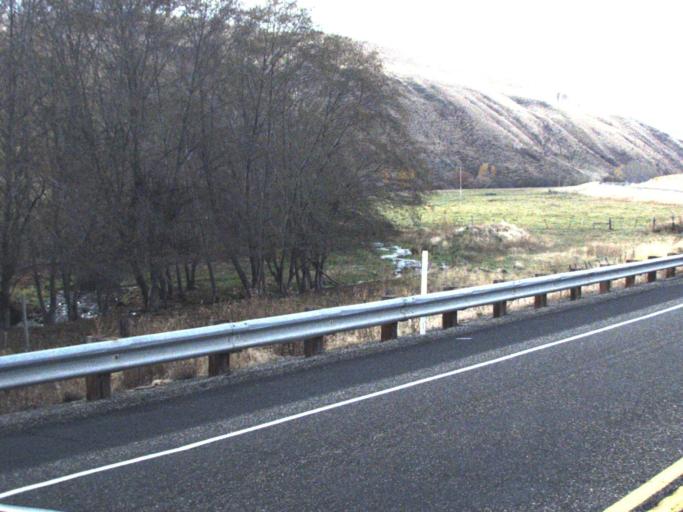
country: US
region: Washington
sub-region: Asotin County
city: Clarkston Heights-Vineland
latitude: 46.4261
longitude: -117.2931
